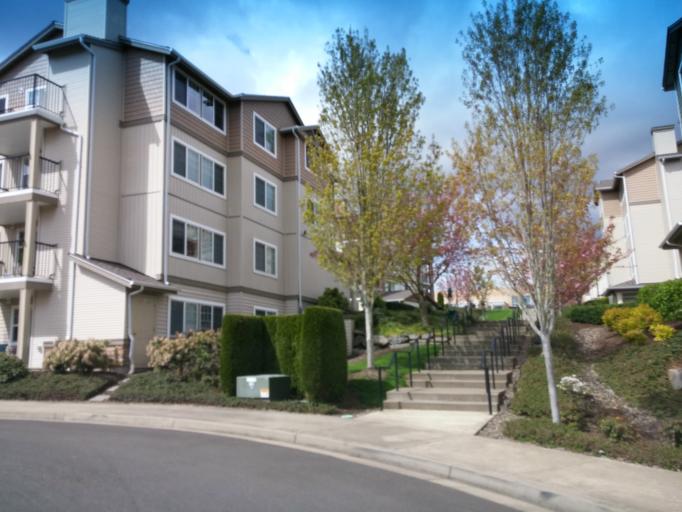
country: US
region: Oregon
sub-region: Washington County
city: Cedar Mill
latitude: 45.5216
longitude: -122.7981
